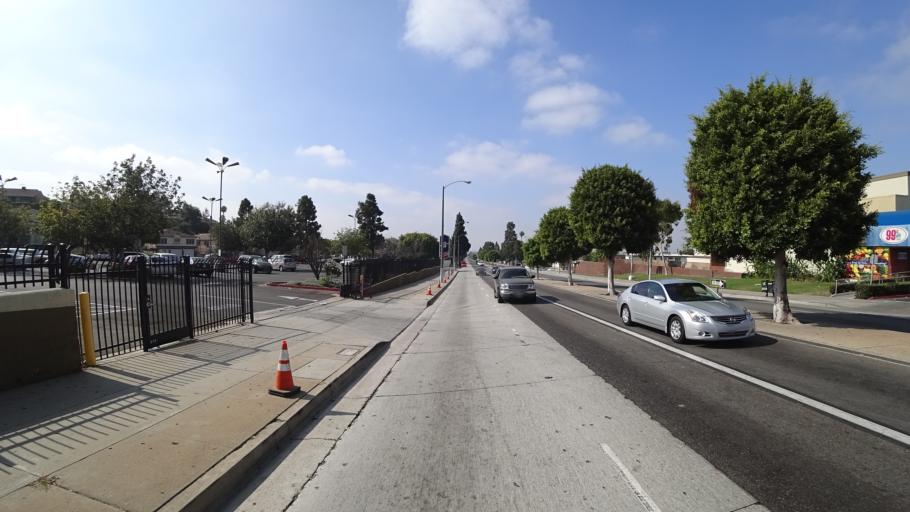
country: US
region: California
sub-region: Los Angeles County
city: Westmont
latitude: 33.9446
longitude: -118.3264
